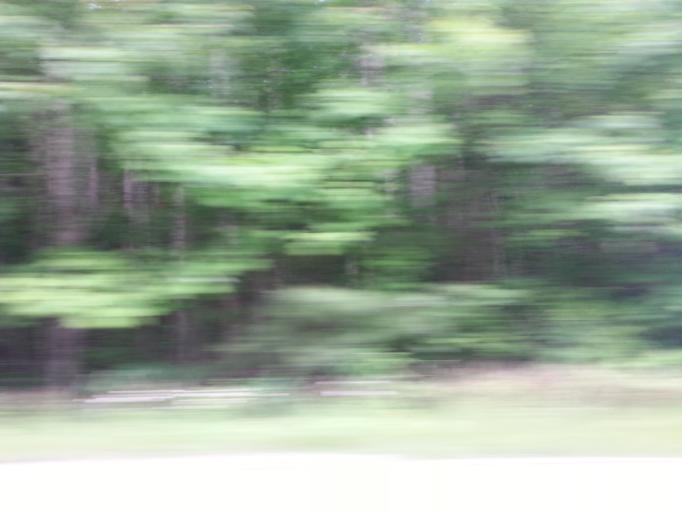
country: US
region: Georgia
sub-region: Towns County
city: Hiawassee
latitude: 34.8376
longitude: -83.8033
